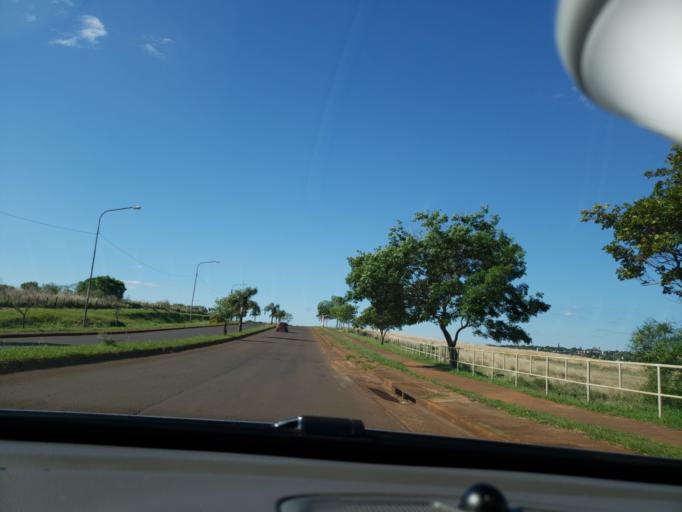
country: AR
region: Misiones
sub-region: Departamento de Capital
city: Posadas
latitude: -27.3884
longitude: -55.9618
